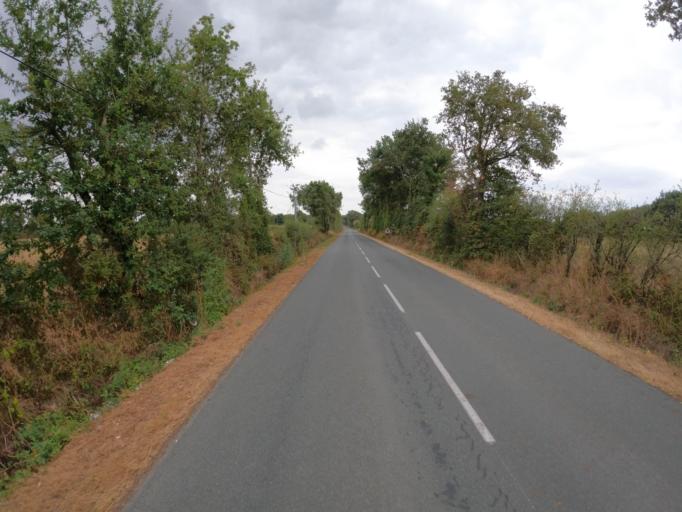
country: FR
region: Pays de la Loire
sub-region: Departement de la Vendee
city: Tiffauges
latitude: 46.9992
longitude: -1.0936
